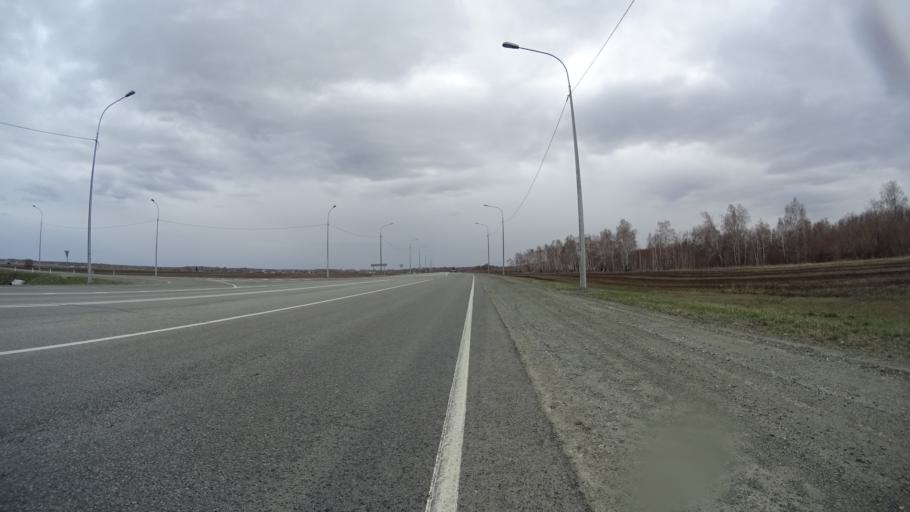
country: RU
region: Chelyabinsk
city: Krasnogorskiy
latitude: 54.6836
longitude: 61.2472
